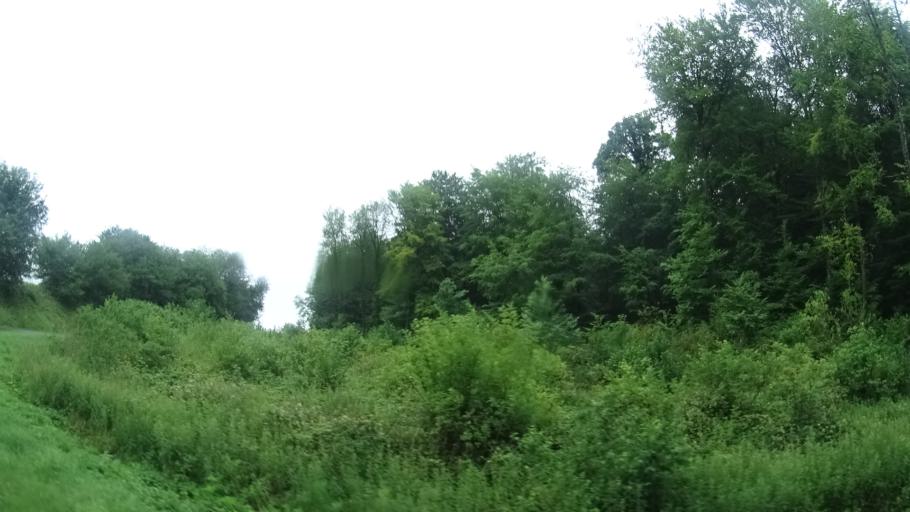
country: BE
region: Wallonia
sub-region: Province du Luxembourg
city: Messancy
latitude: 49.5915
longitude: 5.8031
